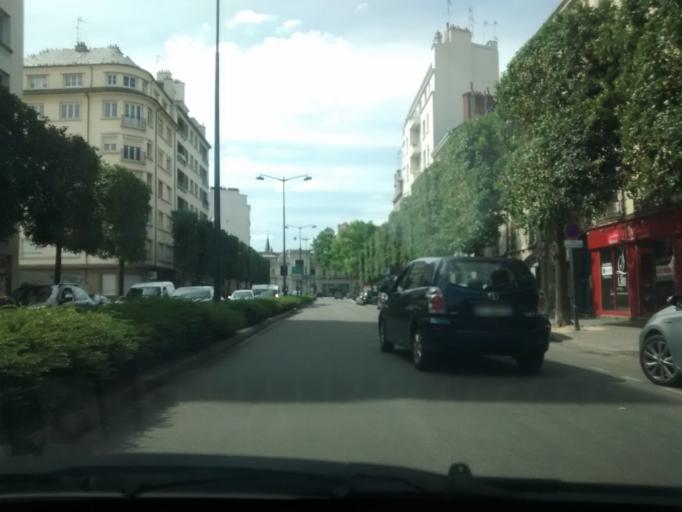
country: FR
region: Brittany
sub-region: Departement d'Ille-et-Vilaine
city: Rennes
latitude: 48.1080
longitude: -1.6824
